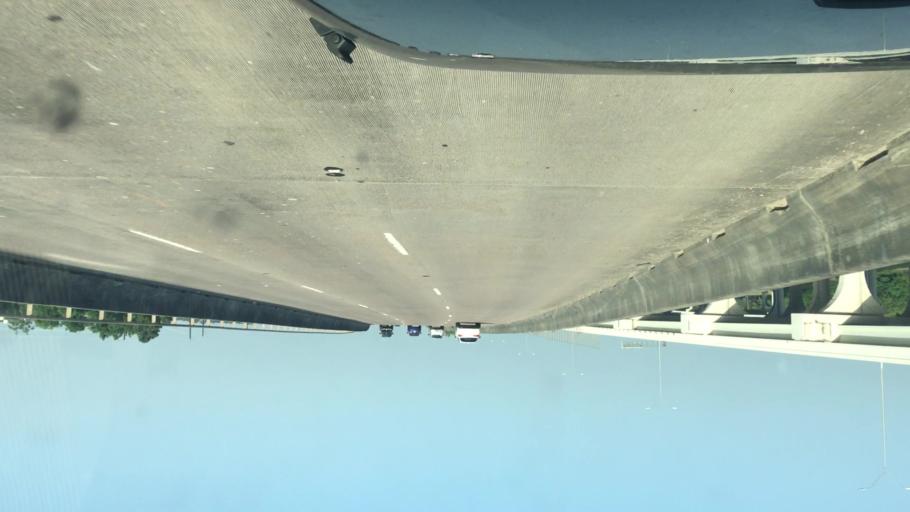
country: US
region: Texas
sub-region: Harris County
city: Atascocita
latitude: 29.9326
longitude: -95.2080
